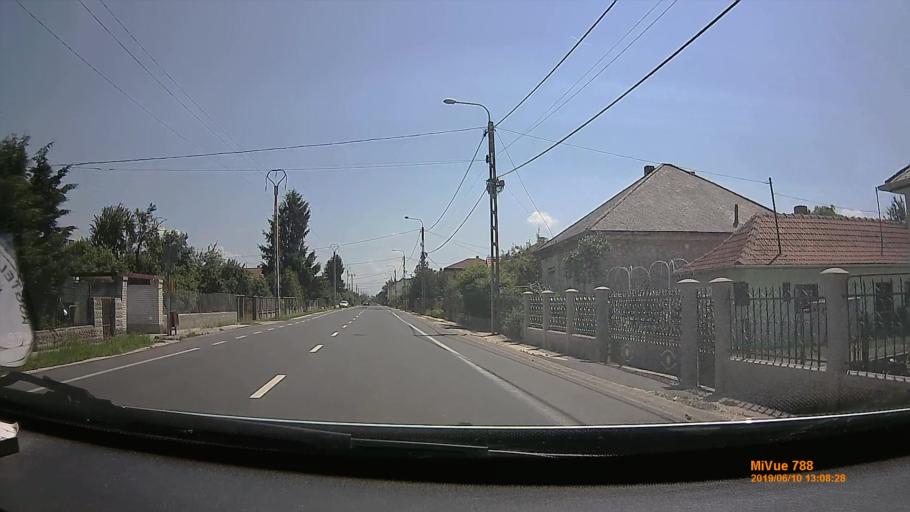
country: HU
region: Borsod-Abauj-Zemplen
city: Hernadnemeti
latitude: 48.0798
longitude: 20.9721
